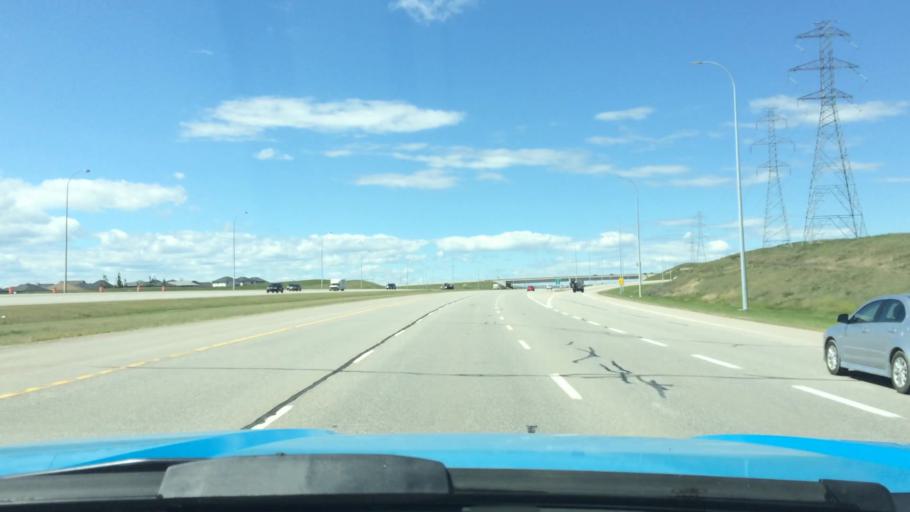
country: CA
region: Alberta
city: Calgary
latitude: 51.1734
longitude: -114.0593
